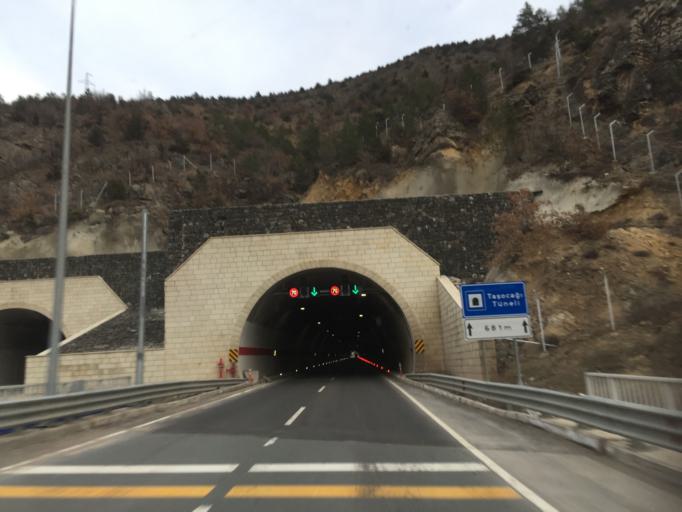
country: TR
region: Gumushane
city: Gumushkhane
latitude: 40.5179
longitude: 39.4113
